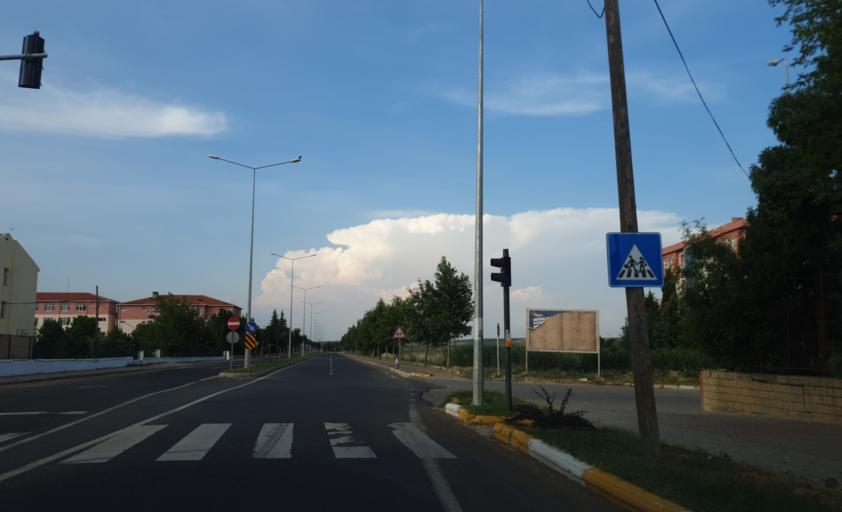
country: TR
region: Tekirdag
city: Hayrabolu
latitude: 41.2203
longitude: 27.1120
